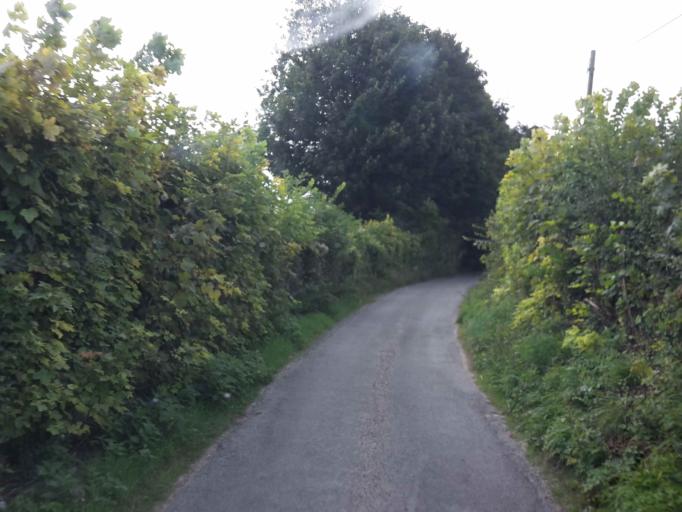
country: GB
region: England
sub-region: West Sussex
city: Washington
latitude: 50.9018
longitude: -0.3711
